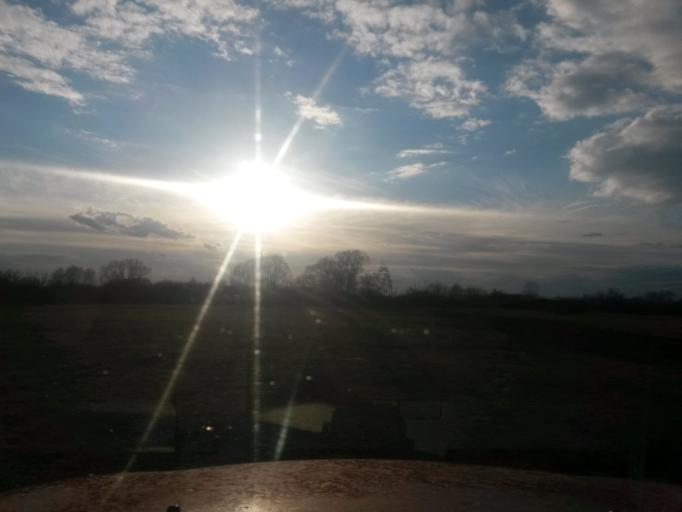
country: SK
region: Kosicky
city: Sobrance
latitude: 48.7024
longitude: 22.0748
